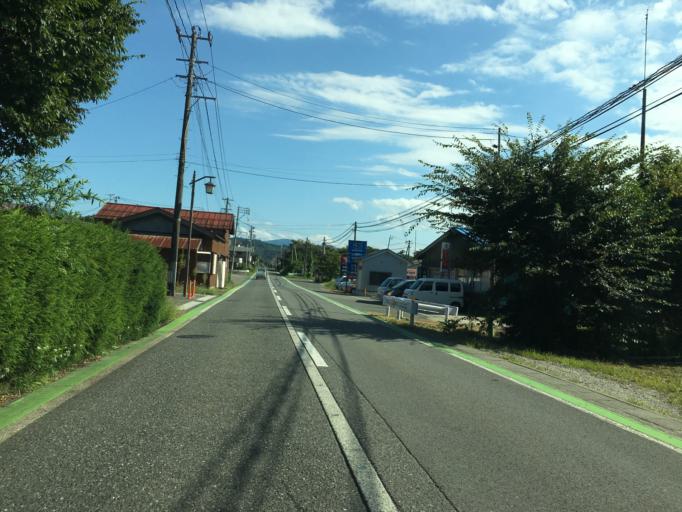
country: JP
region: Niigata
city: Suibara
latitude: 37.6744
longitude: 139.4645
